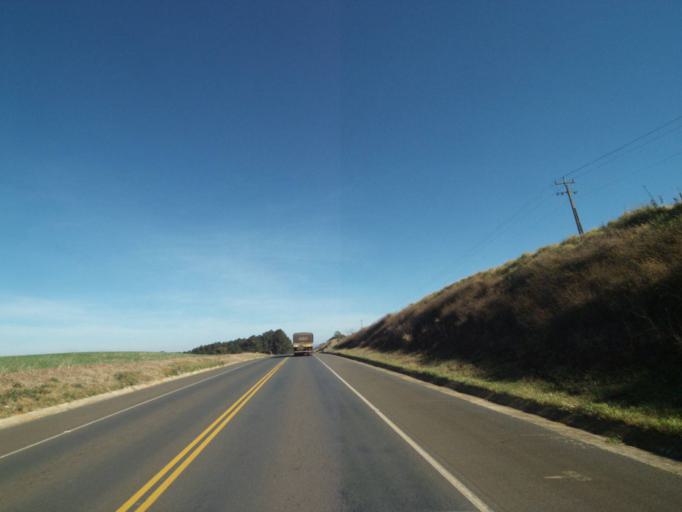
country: BR
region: Parana
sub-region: Tibagi
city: Tibagi
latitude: -24.3628
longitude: -50.3218
